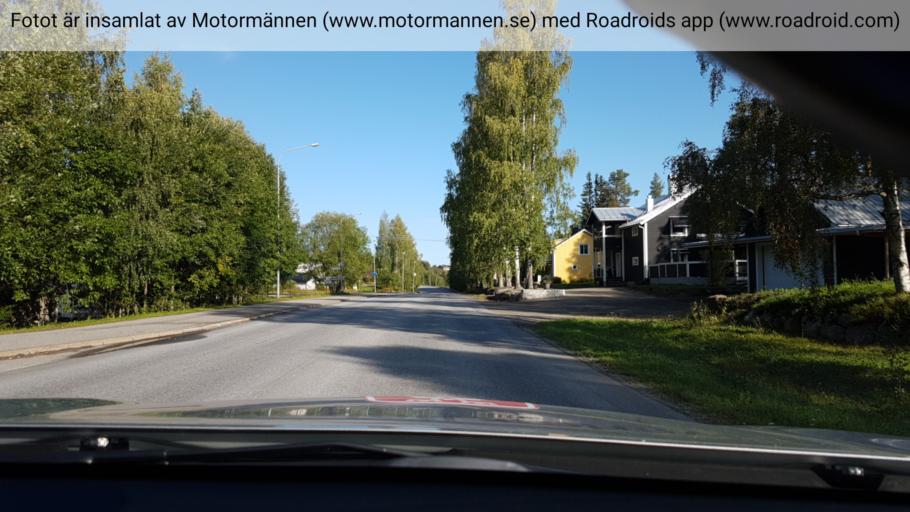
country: SE
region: Vaesterbotten
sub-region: Lycksele Kommun
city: Lycksele
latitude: 64.5821
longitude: 18.6822
